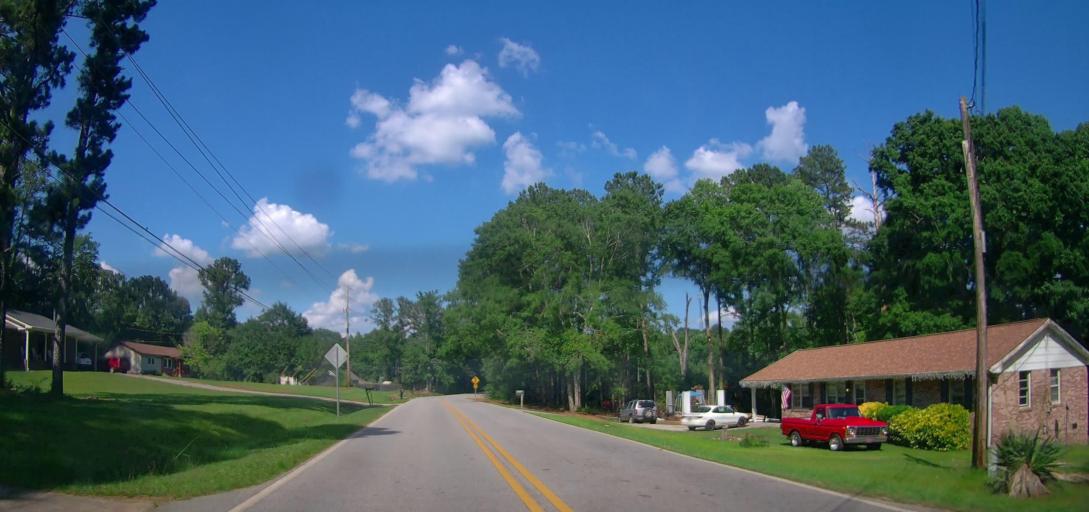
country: US
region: Georgia
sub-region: Spalding County
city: East Griffin
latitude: 33.2907
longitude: -84.2108
